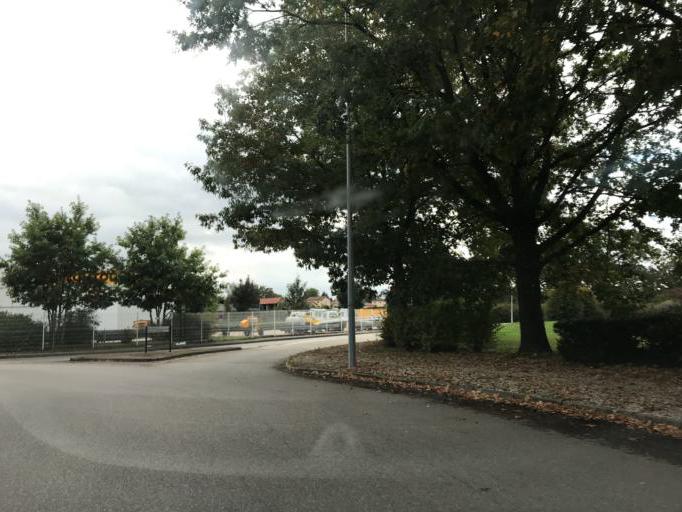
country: FR
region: Rhone-Alpes
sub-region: Departement de l'Ain
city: Saint-Denis-les-Bourg
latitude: 46.2149
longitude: 5.2046
